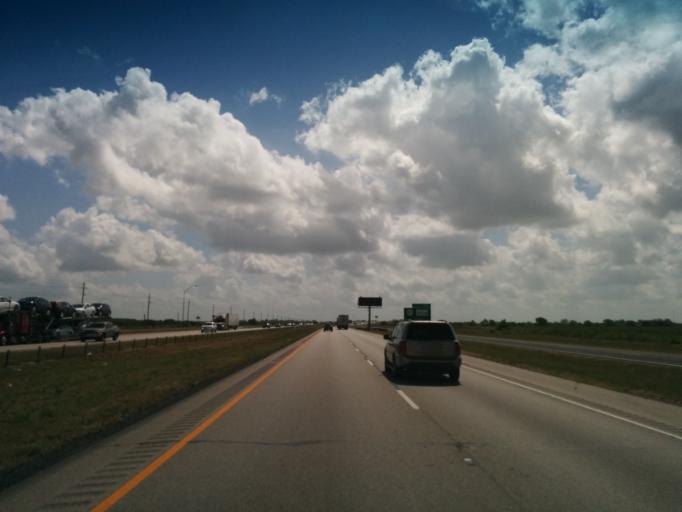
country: US
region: Texas
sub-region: Austin County
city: Sealy
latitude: 29.7623
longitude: -96.1990
